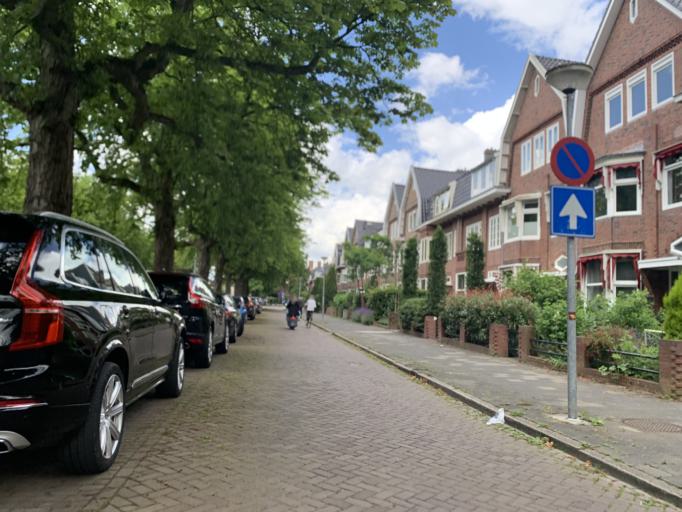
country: NL
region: Groningen
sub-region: Gemeente Groningen
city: Groningen
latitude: 53.1949
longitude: 6.5822
